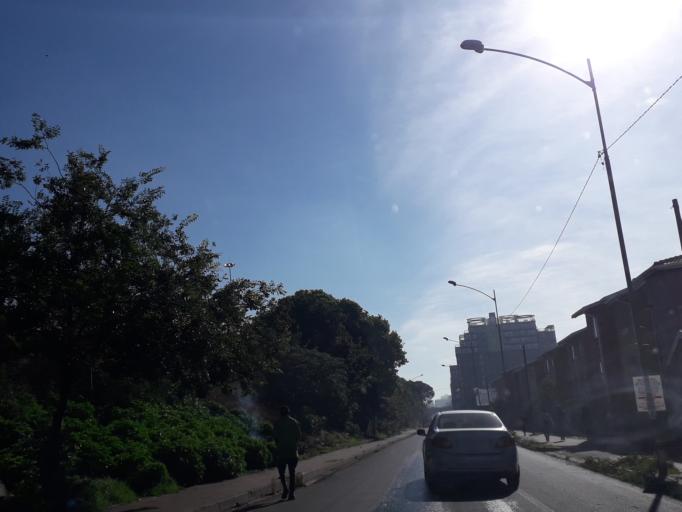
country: ZA
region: Gauteng
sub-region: City of Johannesburg Metropolitan Municipality
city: Johannesburg
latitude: -26.2008
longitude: 28.0237
